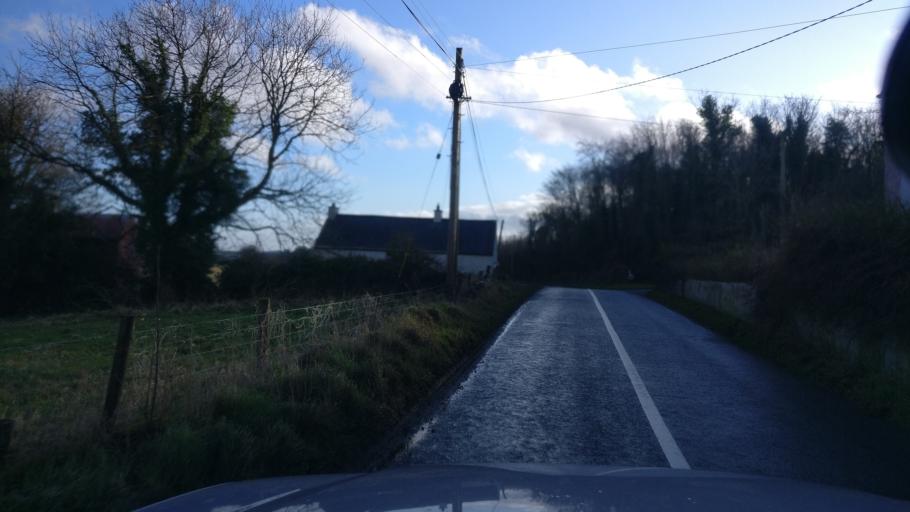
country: IE
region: Connaught
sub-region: County Galway
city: Loughrea
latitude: 53.2573
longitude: -8.6260
